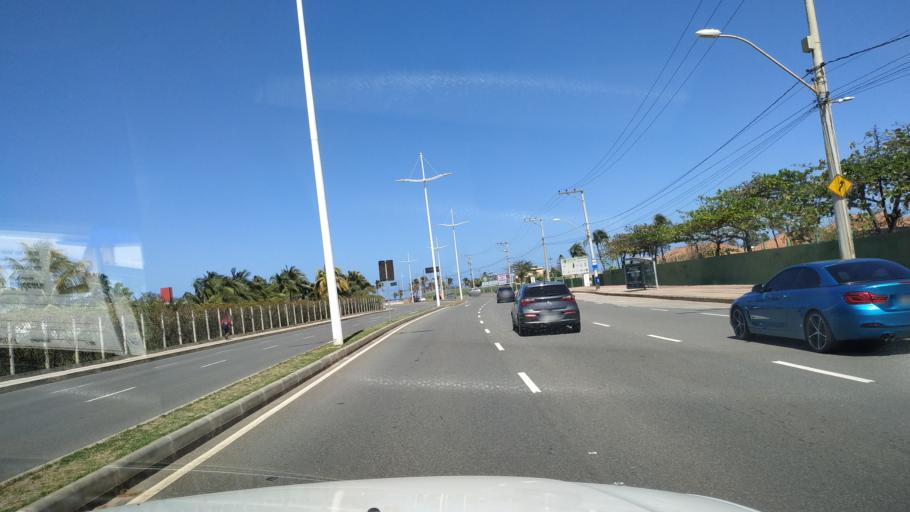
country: BR
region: Bahia
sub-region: Lauro De Freitas
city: Lauro de Freitas
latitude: -12.9518
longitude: -38.3850
